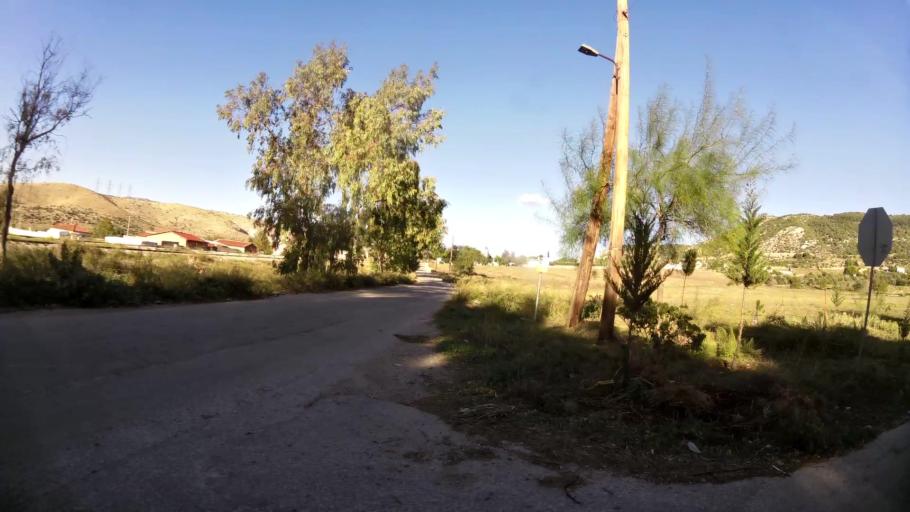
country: GR
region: Attica
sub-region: Nomarchia Athinas
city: Skaramangas
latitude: 38.0384
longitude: 23.6319
